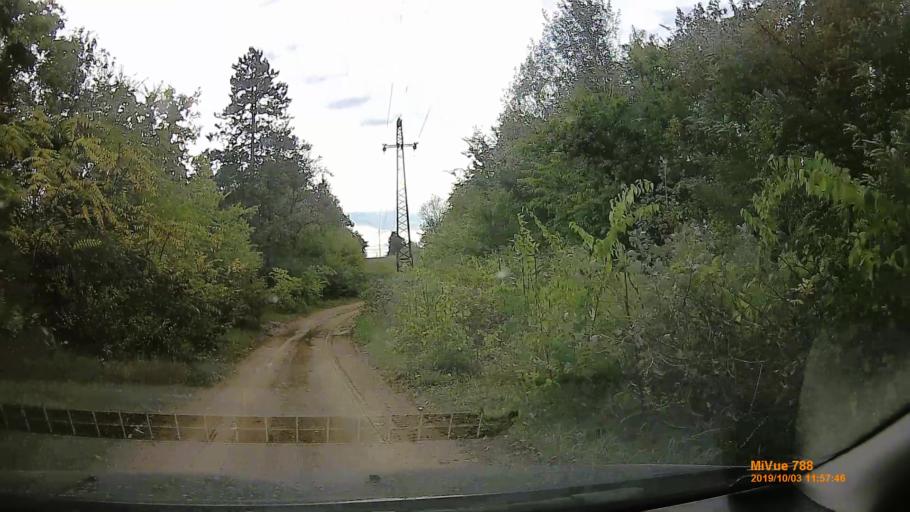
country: HU
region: Pest
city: God
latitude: 47.6724
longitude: 19.1720
